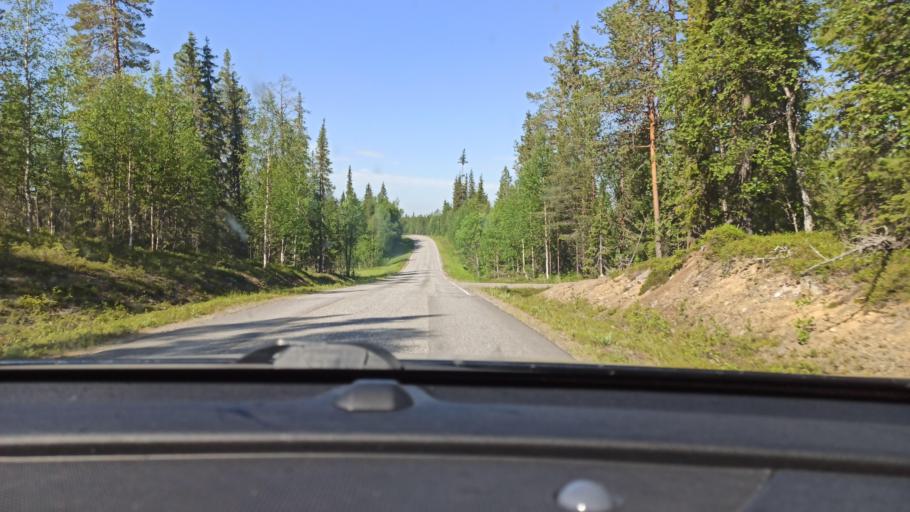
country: FI
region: Lapland
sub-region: Tunturi-Lappi
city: Kolari
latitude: 67.6832
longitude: 24.1283
